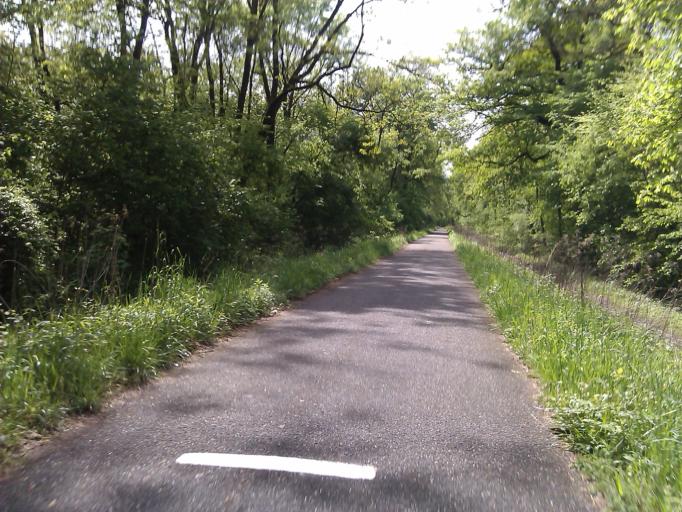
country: FR
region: Alsace
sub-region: Departement du Bas-Rhin
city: La Wantzenau
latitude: 48.6234
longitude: 7.8227
